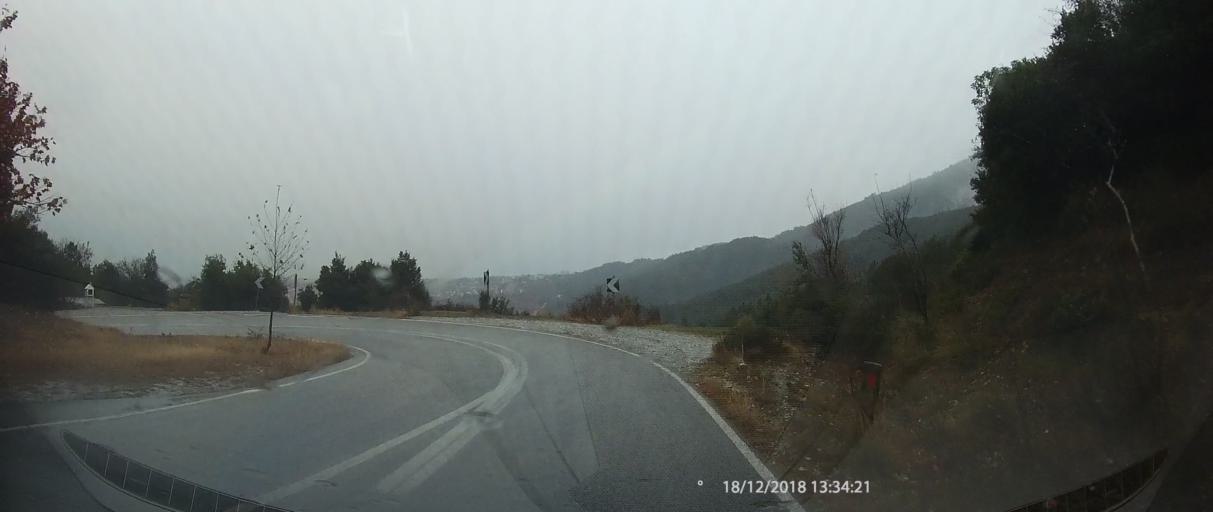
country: GR
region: Central Macedonia
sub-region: Nomos Pierias
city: Litochoro
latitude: 40.1128
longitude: 22.4857
